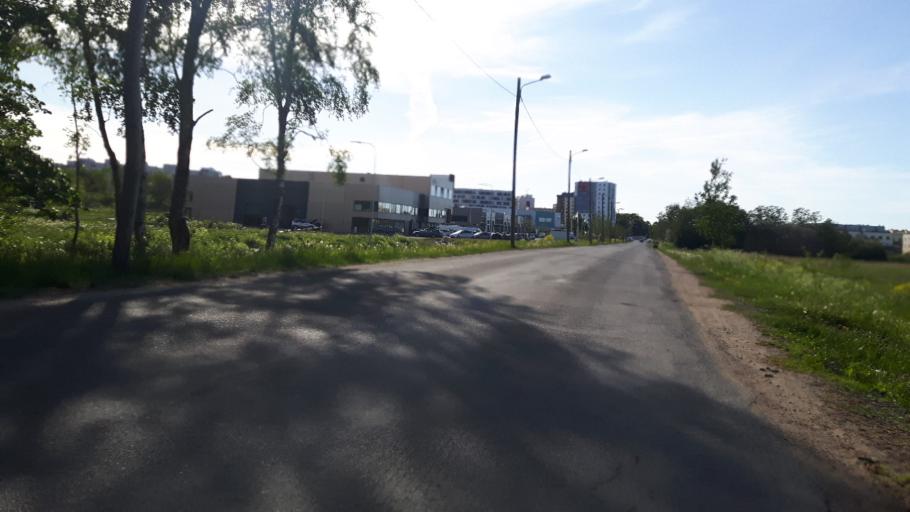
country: EE
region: Harju
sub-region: Tallinna linn
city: Kose
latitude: 59.4508
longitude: 24.8969
